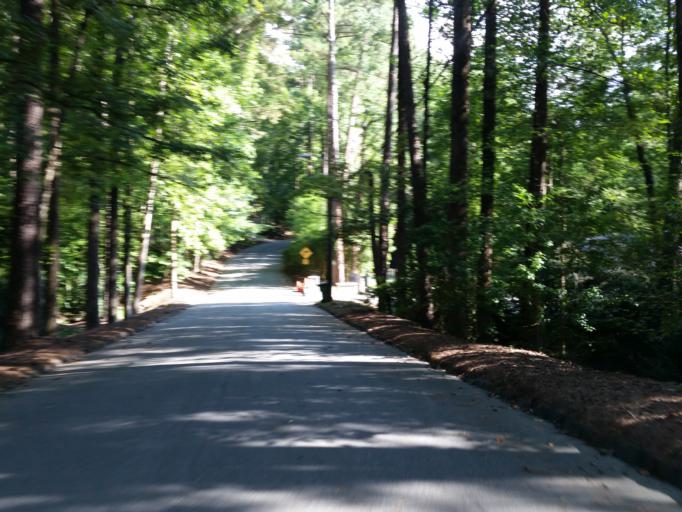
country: US
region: Georgia
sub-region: Cobb County
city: Vinings
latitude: 33.8617
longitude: -84.4346
